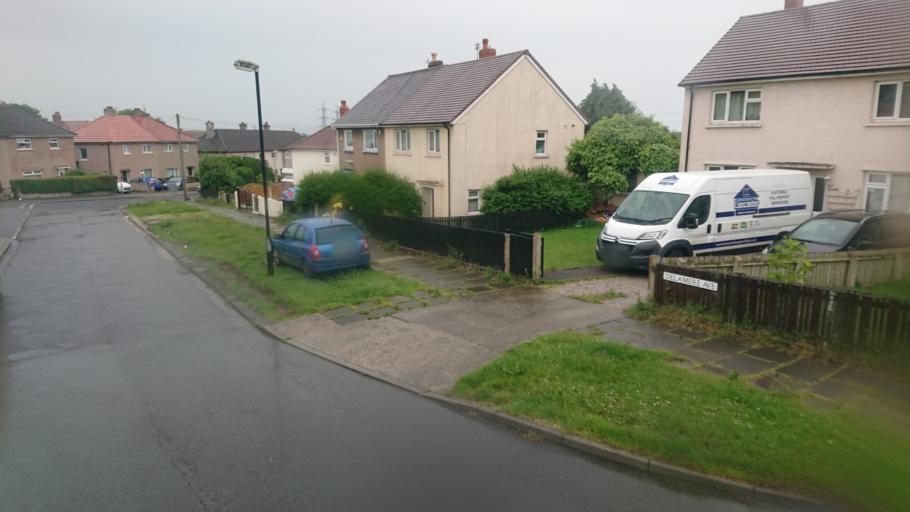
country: GB
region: England
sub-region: Lancashire
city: Morecambe
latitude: 54.0379
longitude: -2.8982
